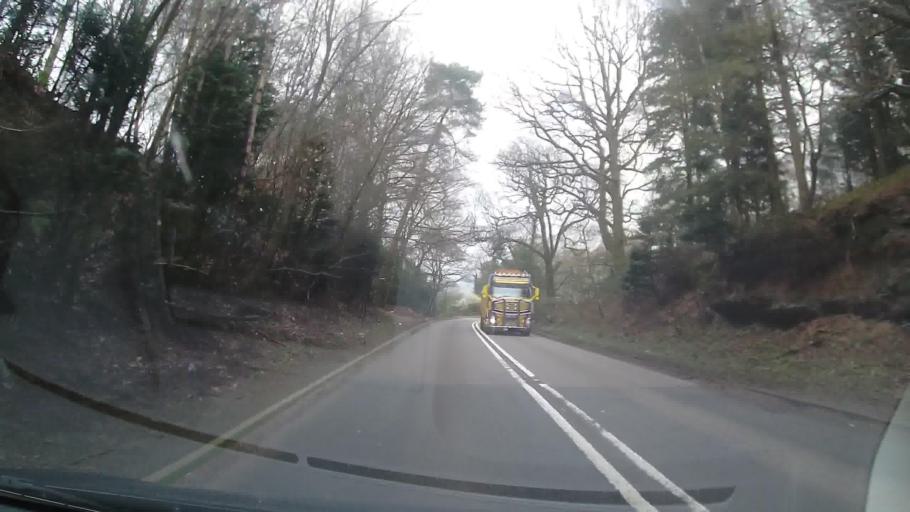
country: GB
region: England
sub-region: Staffordshire
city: Standon
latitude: 52.9537
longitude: -2.3218
